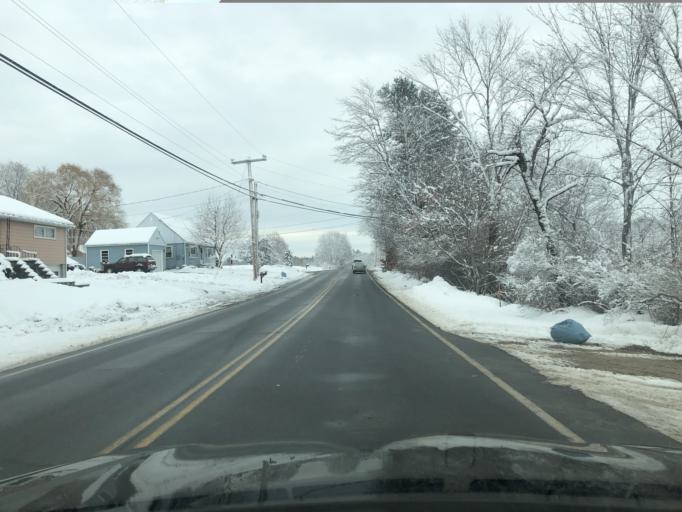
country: US
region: New Hampshire
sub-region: Strafford County
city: Somersworth
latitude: 43.2446
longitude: -70.8627
